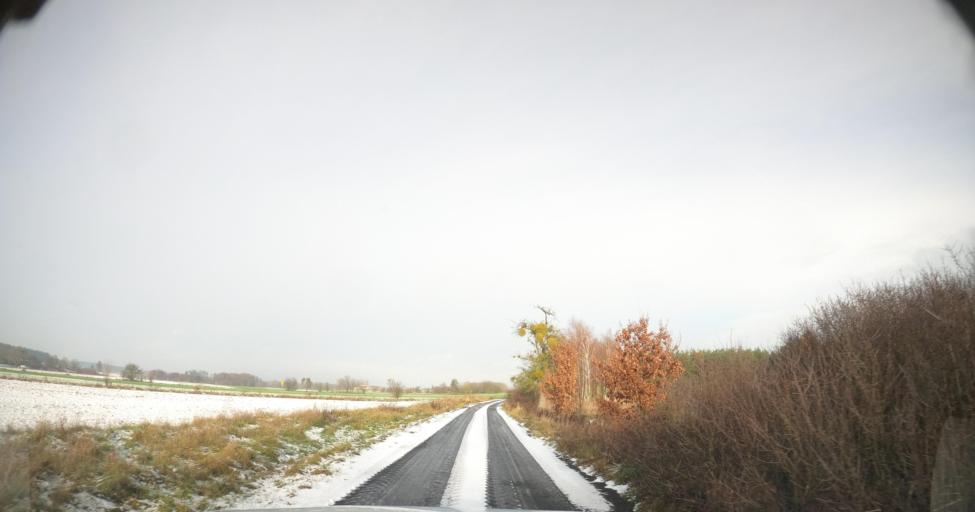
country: PL
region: West Pomeranian Voivodeship
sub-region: Powiat gryfinski
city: Mieszkowice
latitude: 52.7650
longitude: 14.4863
